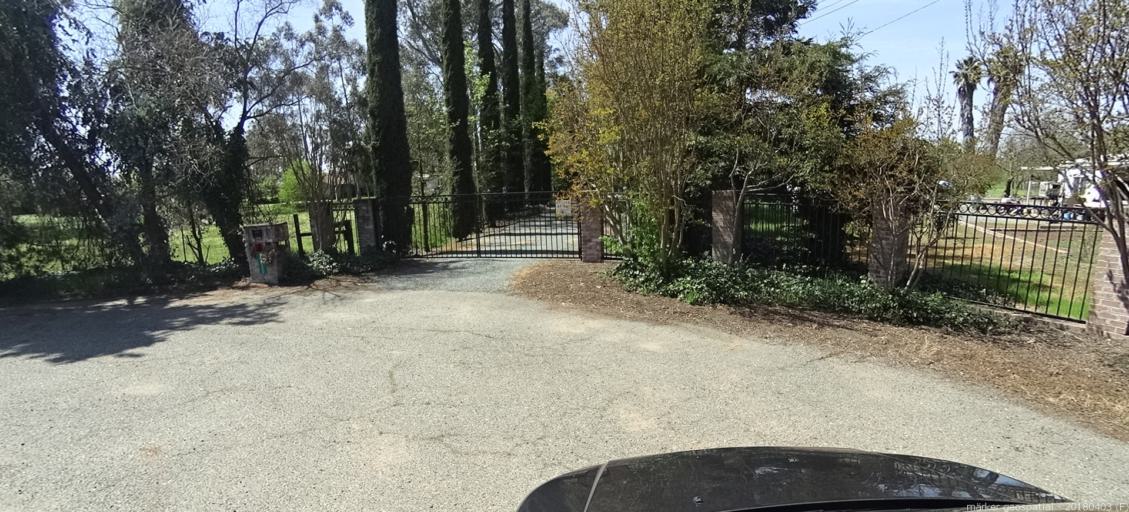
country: US
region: California
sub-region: Sacramento County
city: Wilton
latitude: 38.3933
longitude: -121.2468
